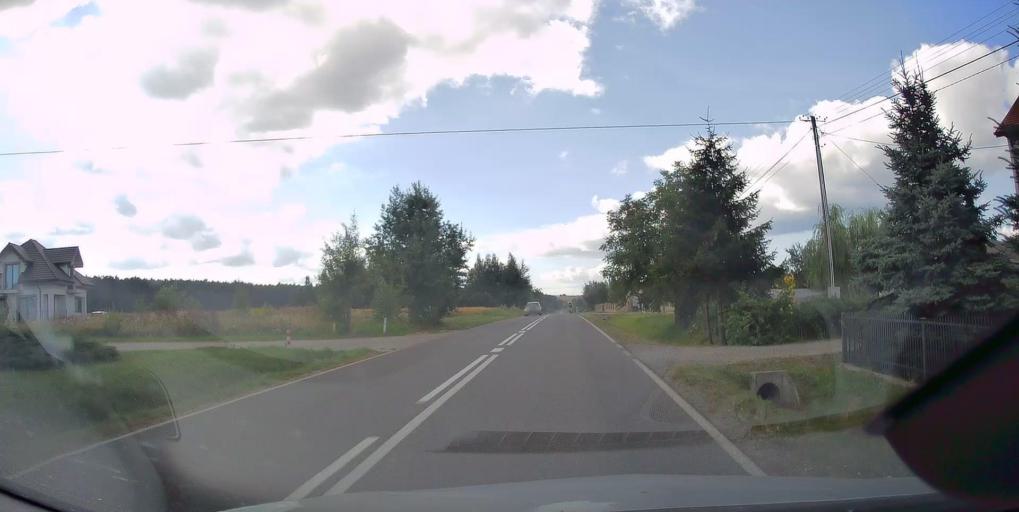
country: PL
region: Swietokrzyskie
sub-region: Powiat kielecki
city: Bodzentyn
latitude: 50.9115
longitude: 21.0018
